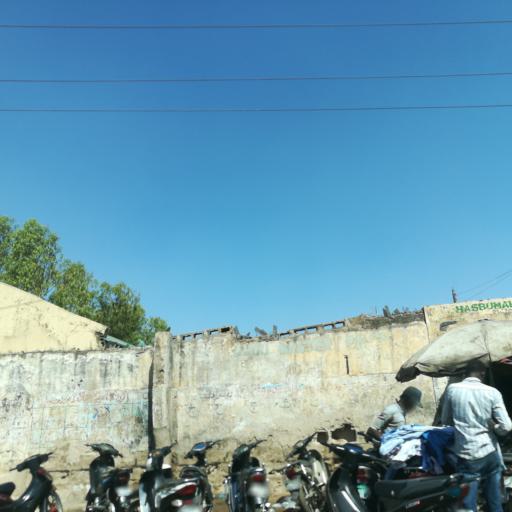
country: NG
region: Kano
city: Kano
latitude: 11.9966
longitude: 8.5304
